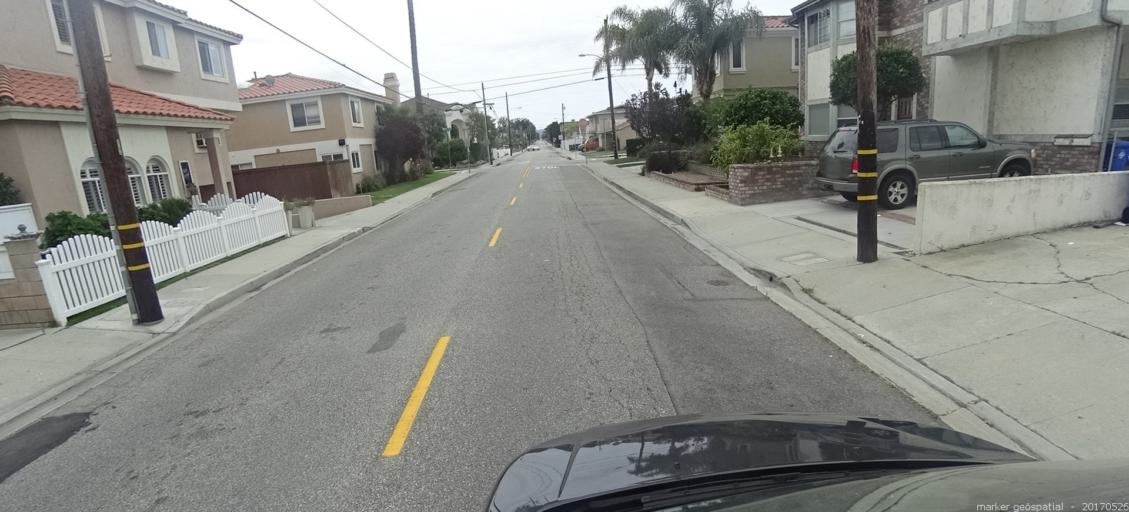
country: US
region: California
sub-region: Los Angeles County
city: Lawndale
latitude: 33.8871
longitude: -118.3729
